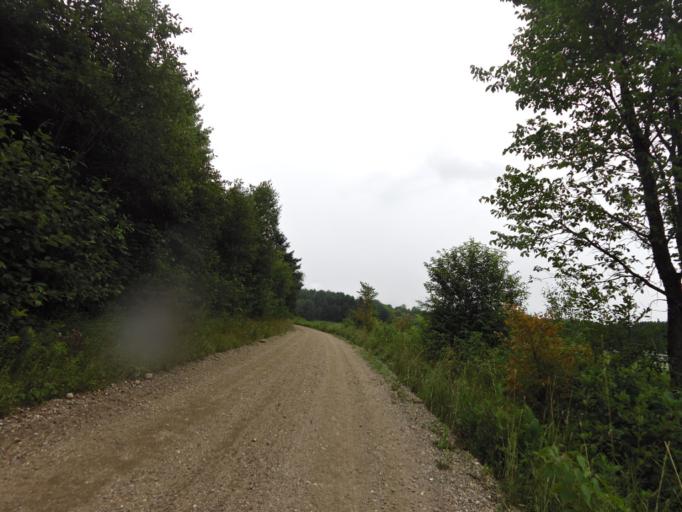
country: CA
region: Quebec
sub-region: Outaouais
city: Wakefield
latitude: 45.6029
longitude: -76.0265
